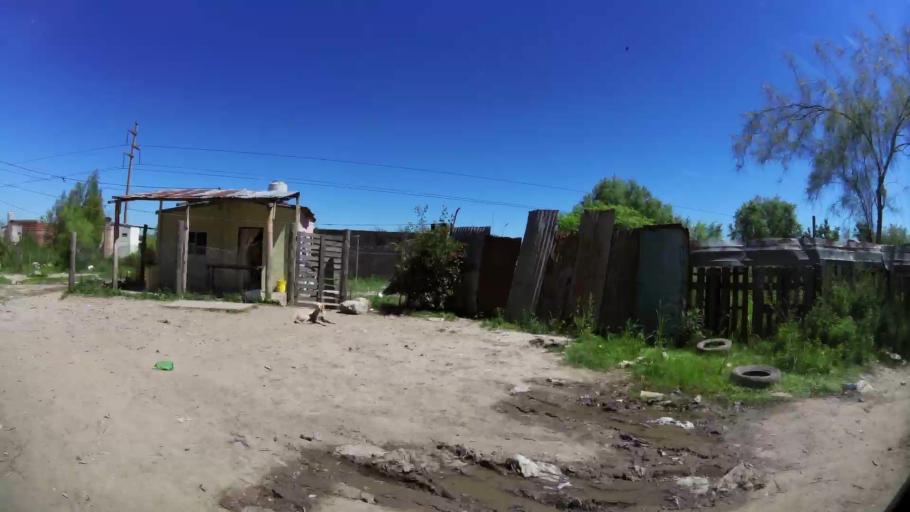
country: AR
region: Santa Fe
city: Santa Fe de la Vera Cruz
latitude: -31.6312
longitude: -60.7244
